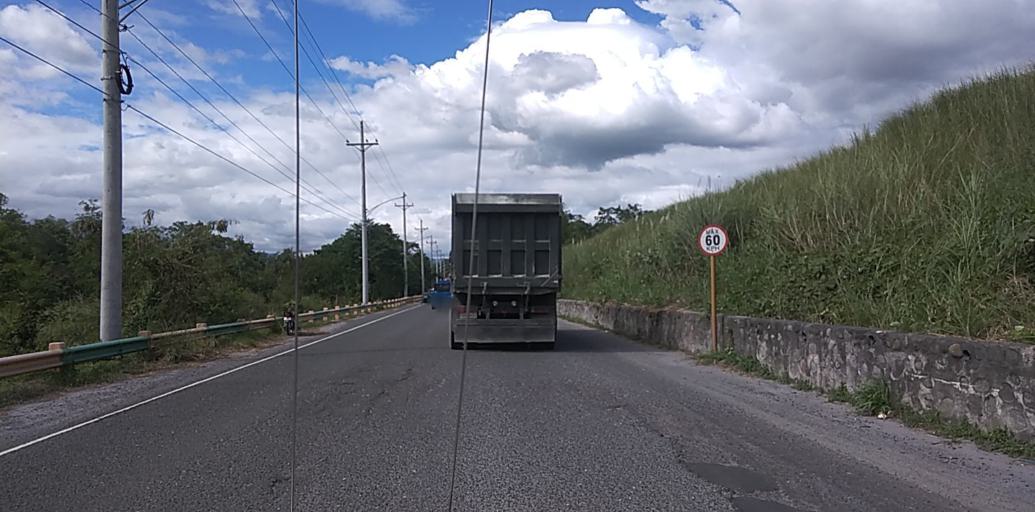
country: PH
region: Central Luzon
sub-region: Province of Pampanga
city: Dolores
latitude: 15.0899
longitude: 120.5368
